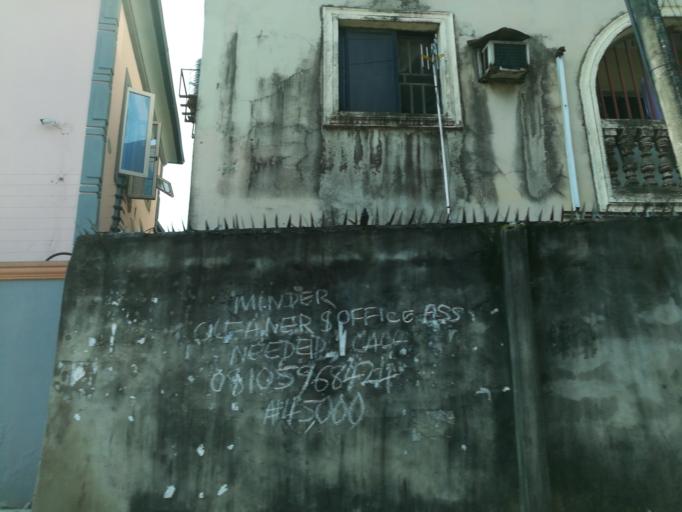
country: NG
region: Rivers
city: Port Harcourt
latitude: 4.8320
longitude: 6.9882
